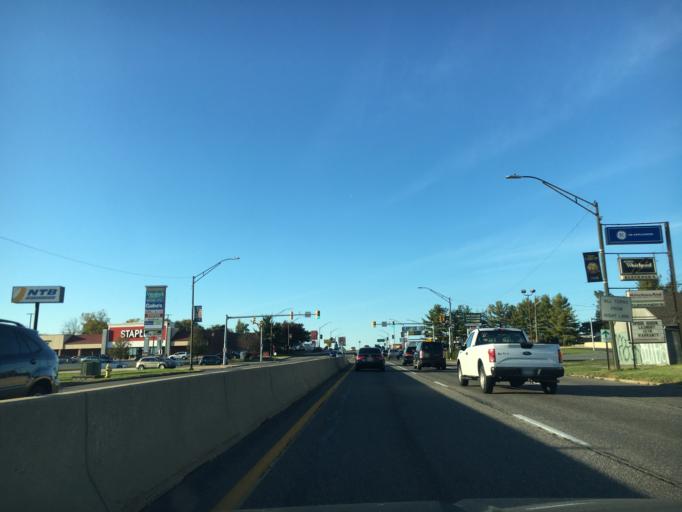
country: US
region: Pennsylvania
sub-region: Lehigh County
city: Fullerton
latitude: 40.6369
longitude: -75.4881
